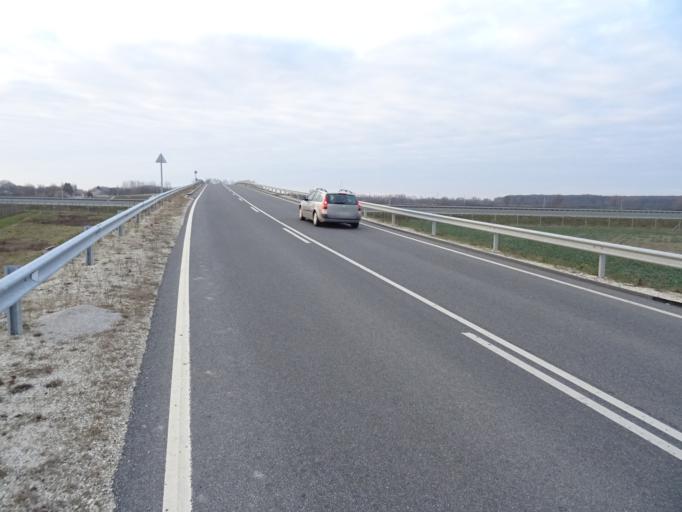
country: HU
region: Gyor-Moson-Sopron
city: Farad
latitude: 47.5356
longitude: 17.2203
